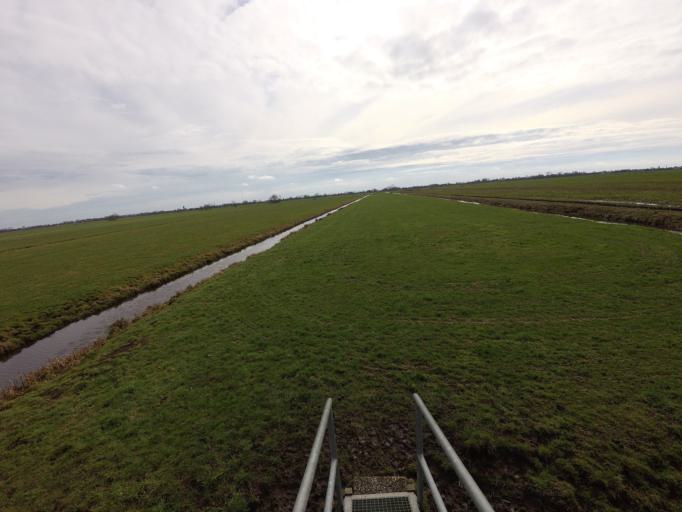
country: NL
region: Utrecht
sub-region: Gemeente Oudewater
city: Oudewater
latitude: 51.9987
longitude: 4.8738
